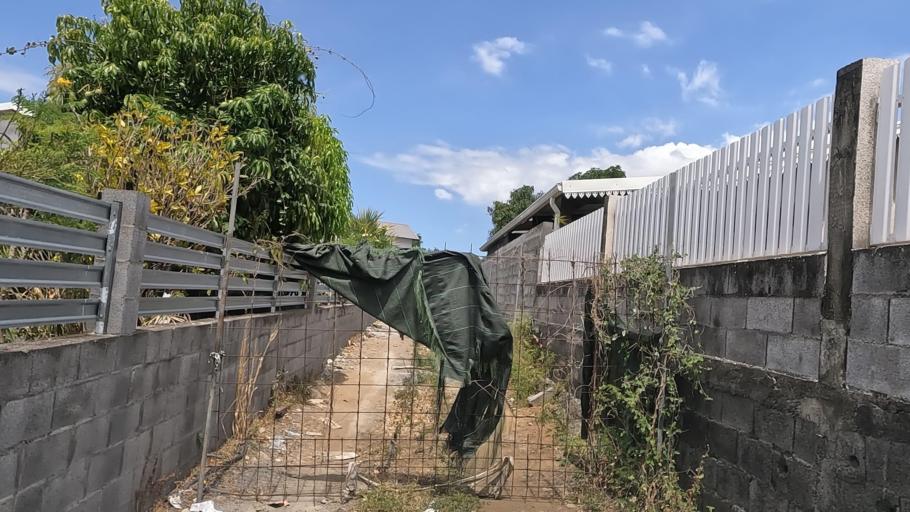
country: RE
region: Reunion
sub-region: Reunion
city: Saint-Louis
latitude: -21.2772
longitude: 55.4497
